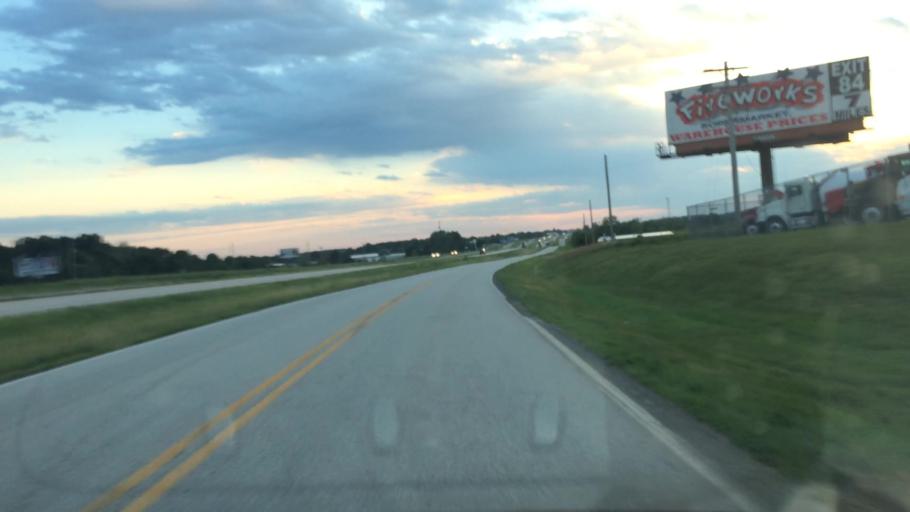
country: US
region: Missouri
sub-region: Greene County
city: Strafford
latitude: 37.2708
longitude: -93.0699
